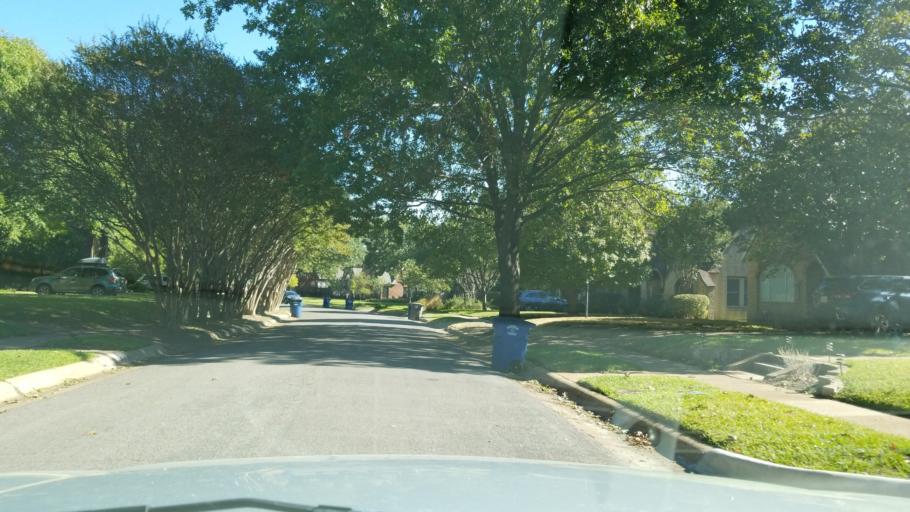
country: US
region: Texas
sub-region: Dallas County
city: Highland Park
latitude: 32.8037
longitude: -96.7420
